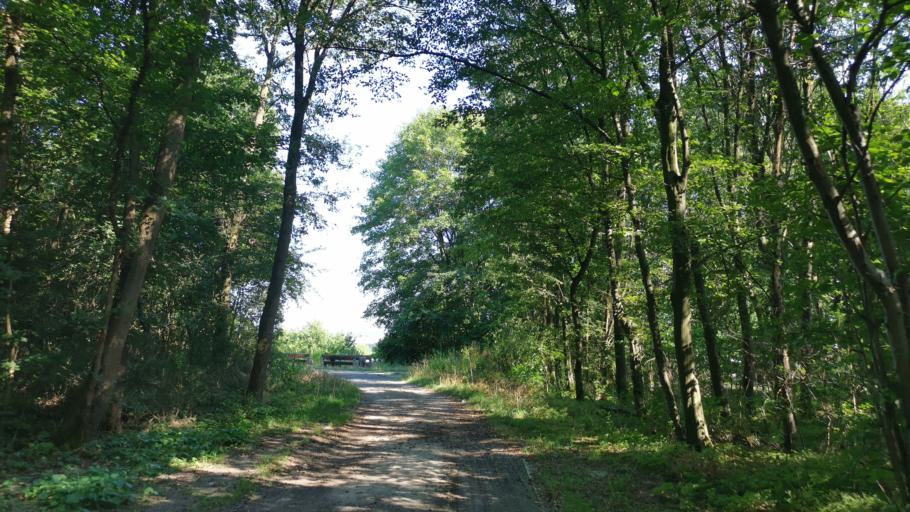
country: DE
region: Bavaria
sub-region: Regierungsbezirk Mittelfranken
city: Nuernberg
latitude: 49.4200
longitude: 11.1135
